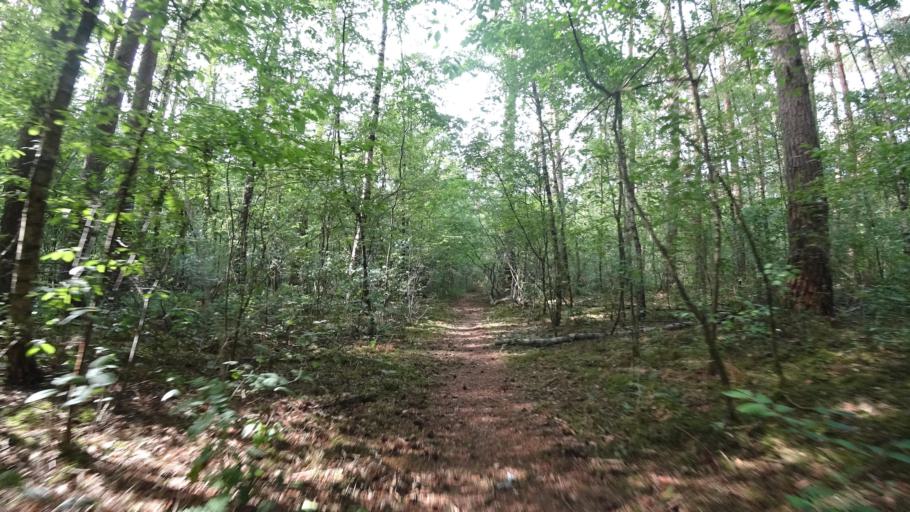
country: DE
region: North Rhine-Westphalia
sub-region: Regierungsbezirk Detmold
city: Verl
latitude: 51.8989
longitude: 8.4573
